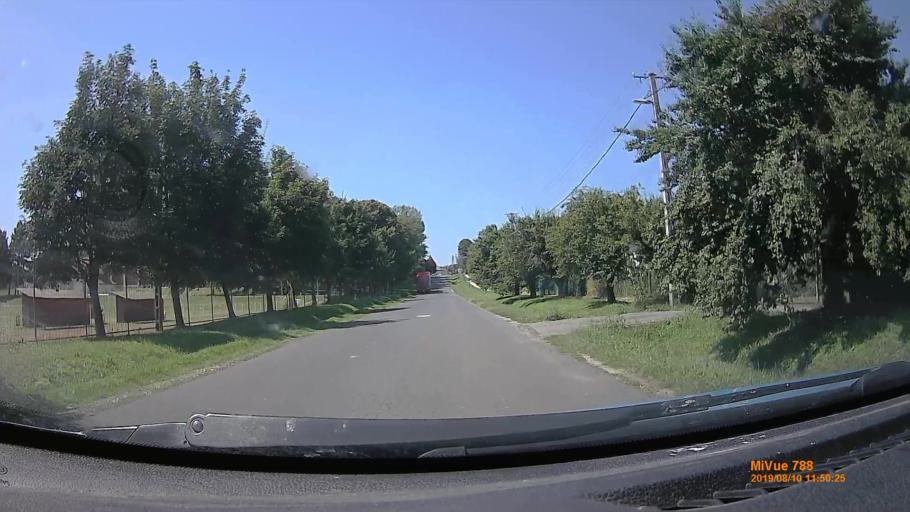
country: HU
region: Somogy
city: Somogyvar
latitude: 46.4929
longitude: 17.7192
